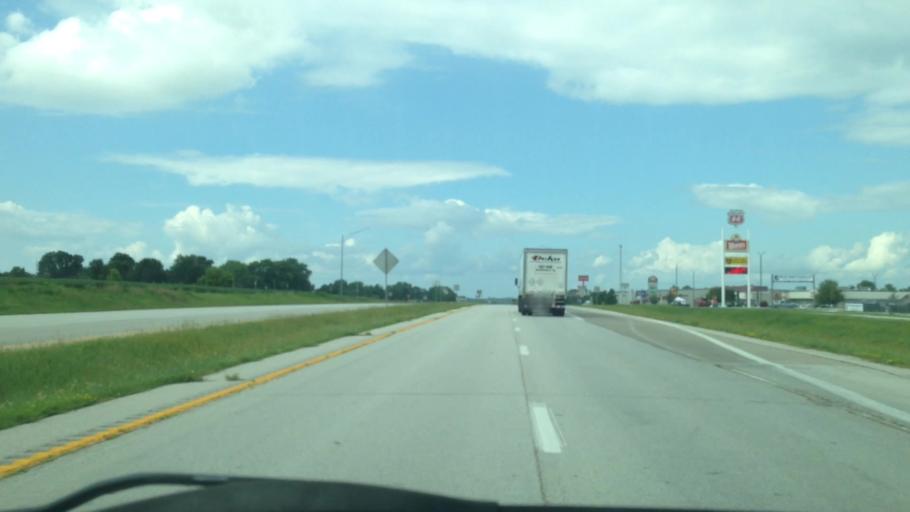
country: US
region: Missouri
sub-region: Marion County
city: Palmyra
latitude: 39.7853
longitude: -91.5177
